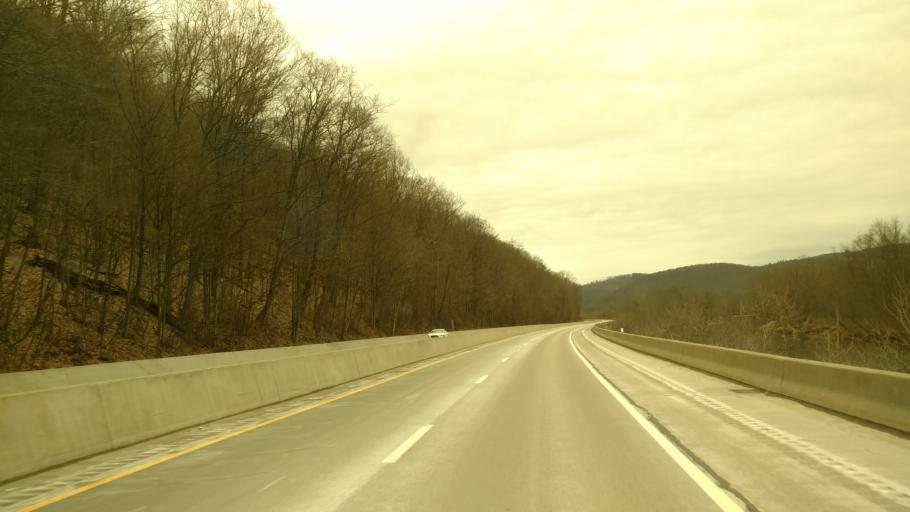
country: US
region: New York
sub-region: Cattaraugus County
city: Salamanca
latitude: 42.1299
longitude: -78.6665
